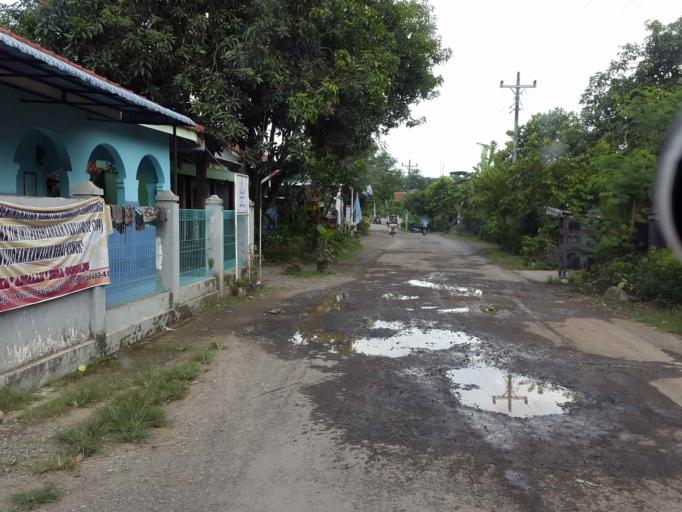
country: ID
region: Central Java
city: Petarukan
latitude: -6.9342
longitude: 109.4472
